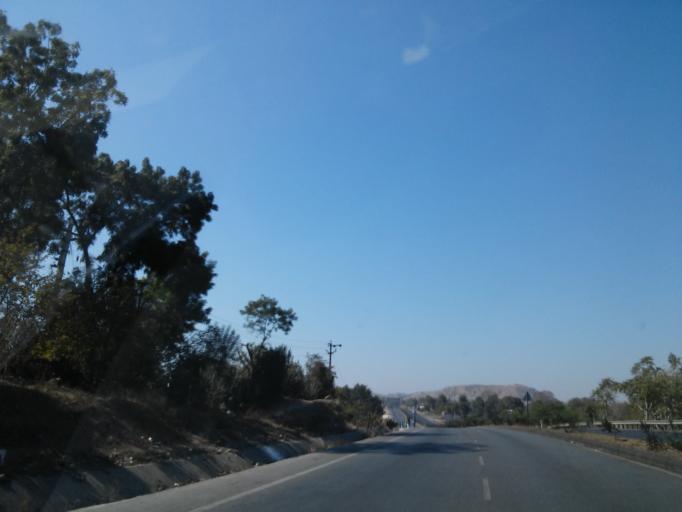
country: IN
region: Rajasthan
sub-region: Dungarpur
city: Dungarpur
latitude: 24.0013
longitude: 73.6458
